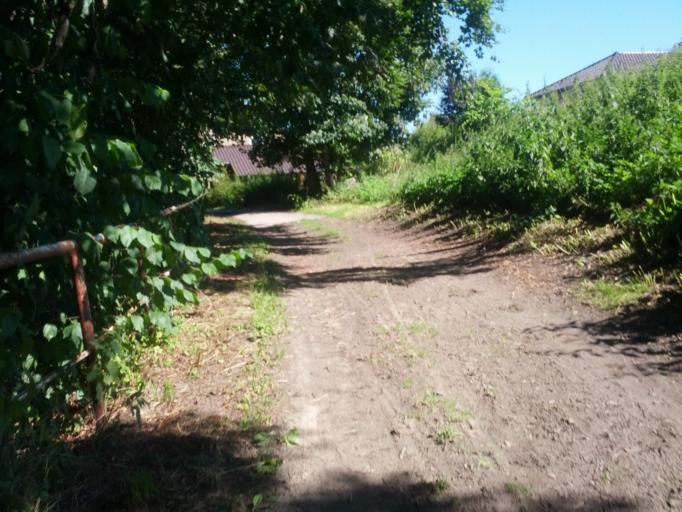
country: DE
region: Mecklenburg-Vorpommern
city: Bastorf
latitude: 54.1143
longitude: 11.6752
